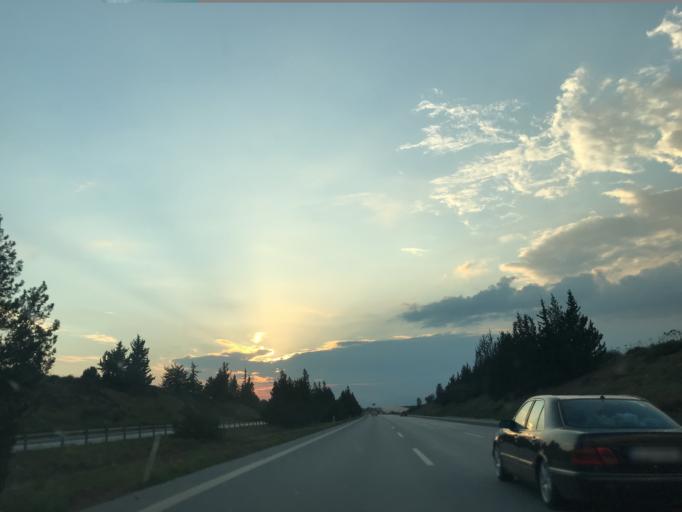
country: TR
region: Mersin
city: Yenice
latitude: 37.0234
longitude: 35.0527
